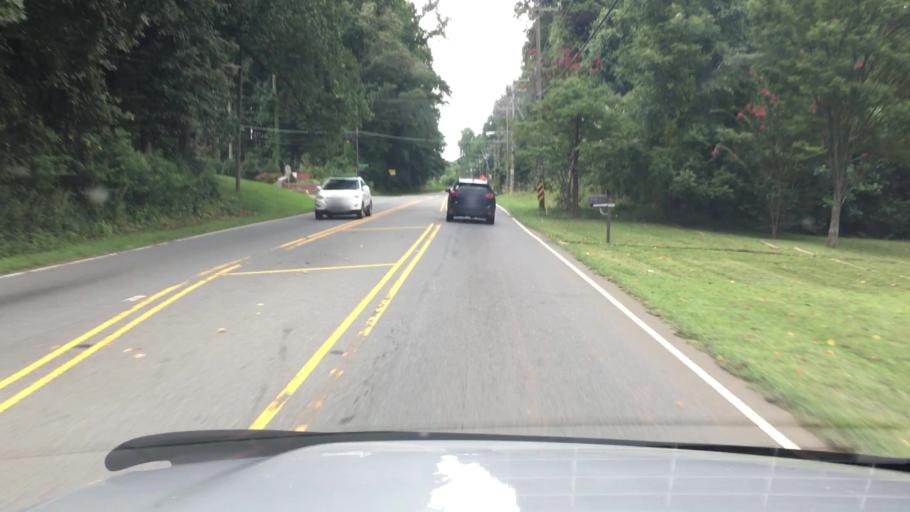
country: US
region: North Carolina
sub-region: Mecklenburg County
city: Charlotte
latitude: 35.3157
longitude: -80.8645
